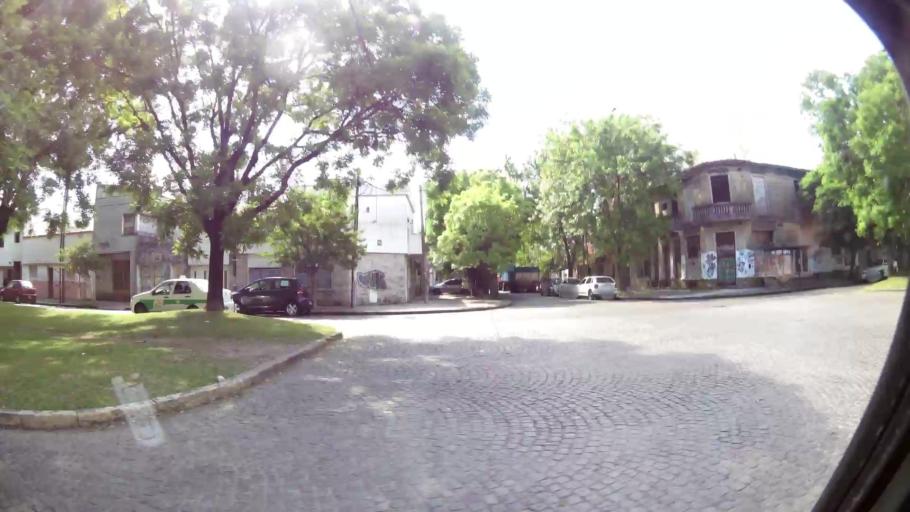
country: AR
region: Buenos Aires
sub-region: Partido de La Plata
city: La Plata
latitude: -34.9279
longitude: -57.9368
